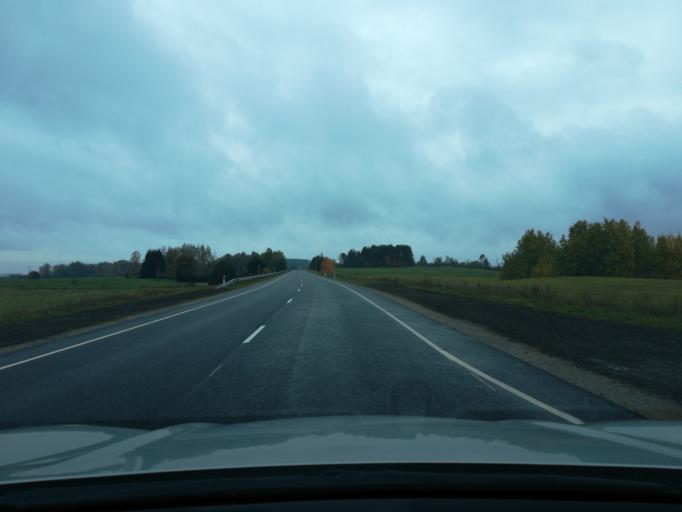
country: EE
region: Ida-Virumaa
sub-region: Johvi vald
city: Johvi
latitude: 59.1313
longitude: 27.3331
